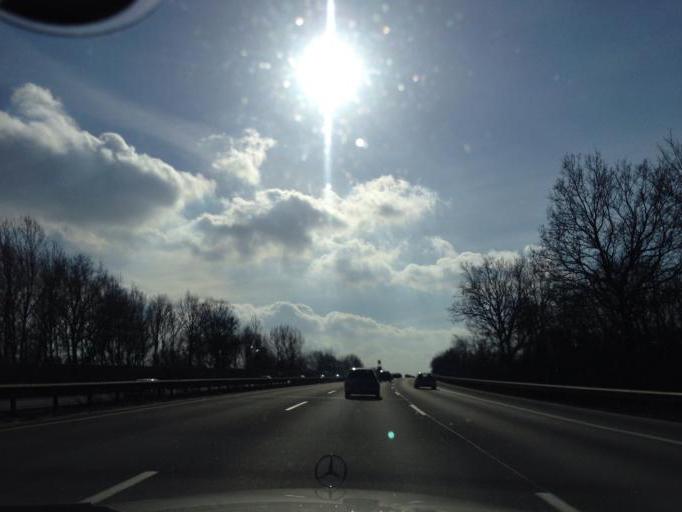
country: DE
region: Hamburg
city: Harburg
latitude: 53.4259
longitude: 10.0346
